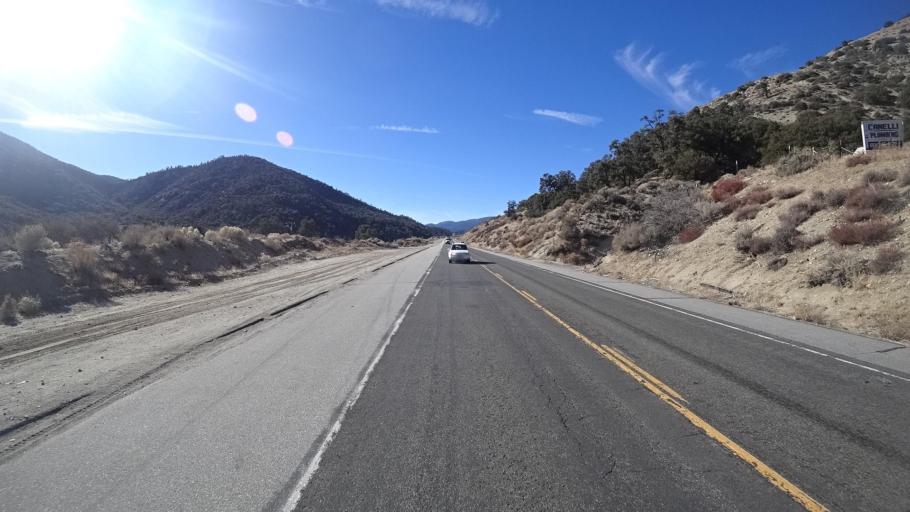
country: US
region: California
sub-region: Kern County
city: Frazier Park
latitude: 34.8211
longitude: -118.9755
